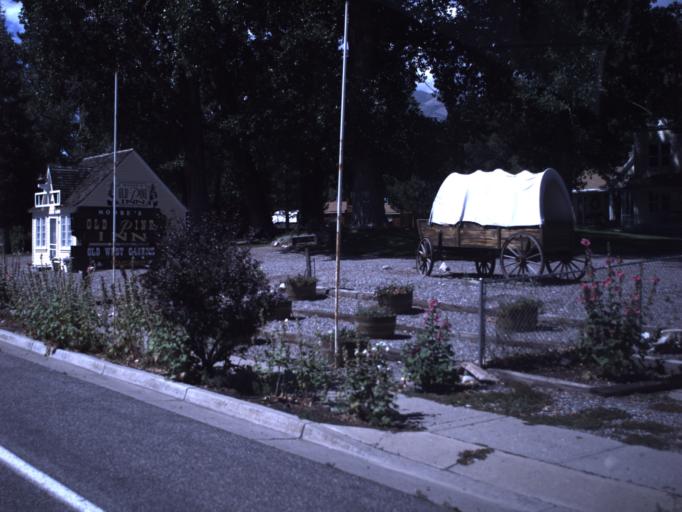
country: US
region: Utah
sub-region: Piute County
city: Junction
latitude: 38.4488
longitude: -112.2304
